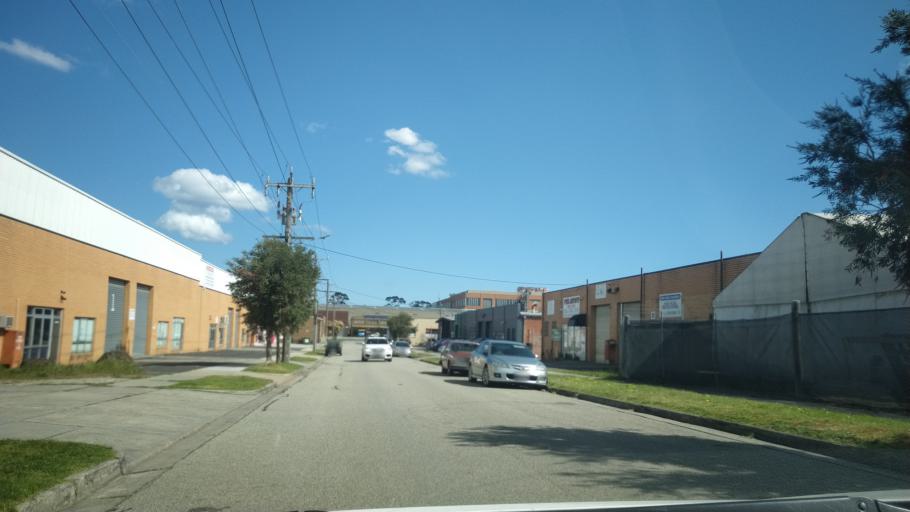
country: AU
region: Victoria
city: Highett
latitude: -37.9384
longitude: 145.0654
